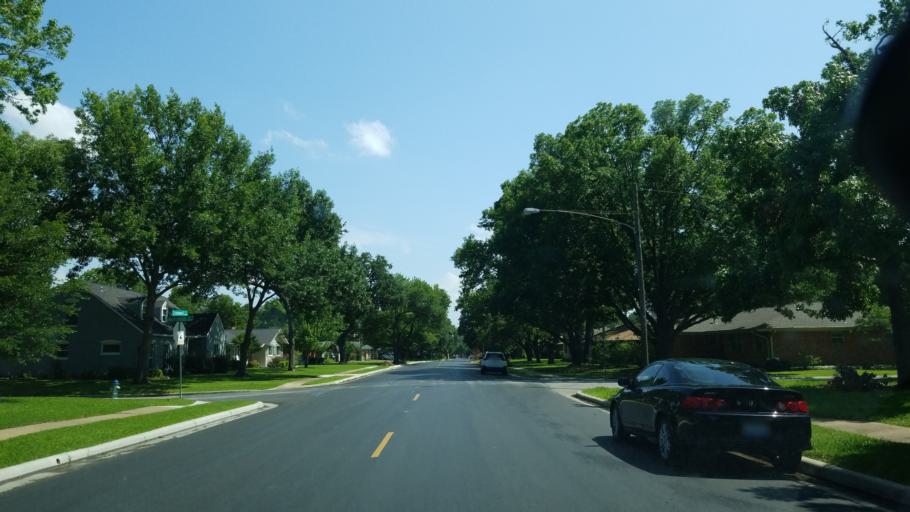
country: US
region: Texas
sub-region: Dallas County
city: Farmers Branch
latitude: 32.8901
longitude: -96.8624
